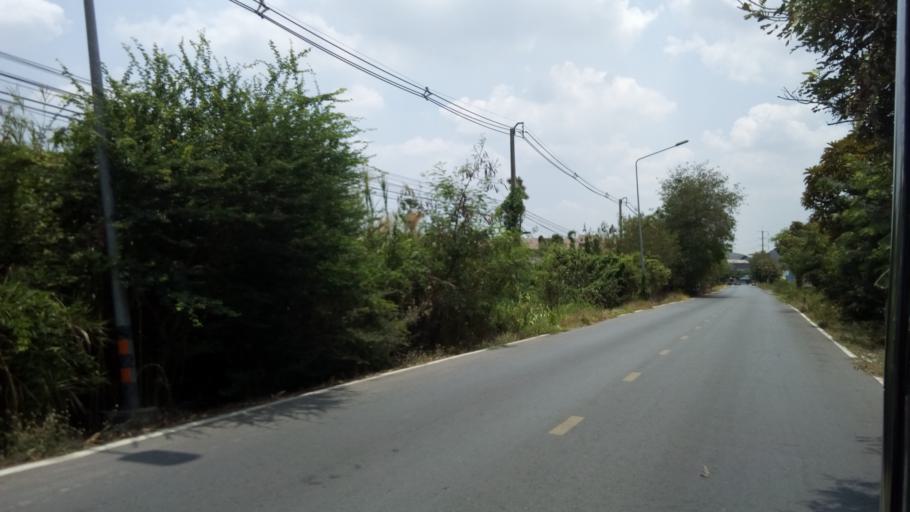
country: TH
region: Pathum Thani
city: Sam Khok
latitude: 14.0825
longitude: 100.5215
